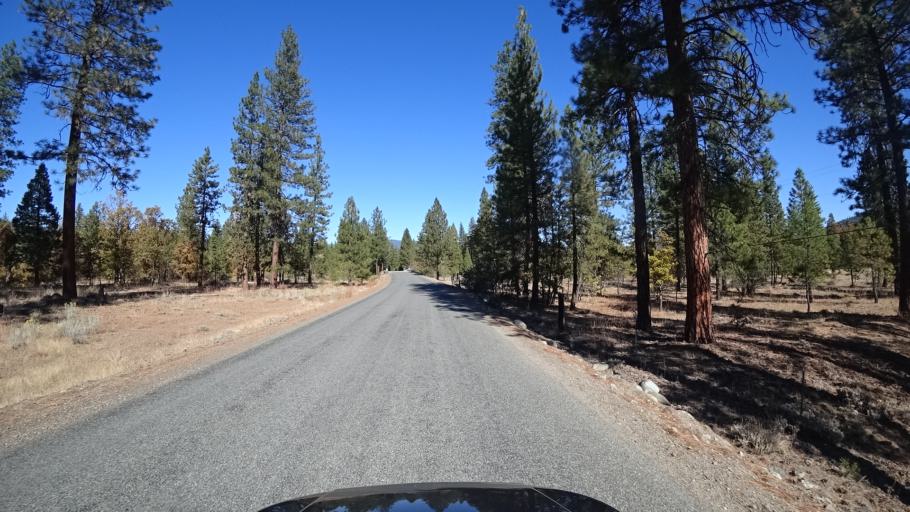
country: US
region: California
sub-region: Siskiyou County
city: Yreka
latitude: 41.5927
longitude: -122.9745
